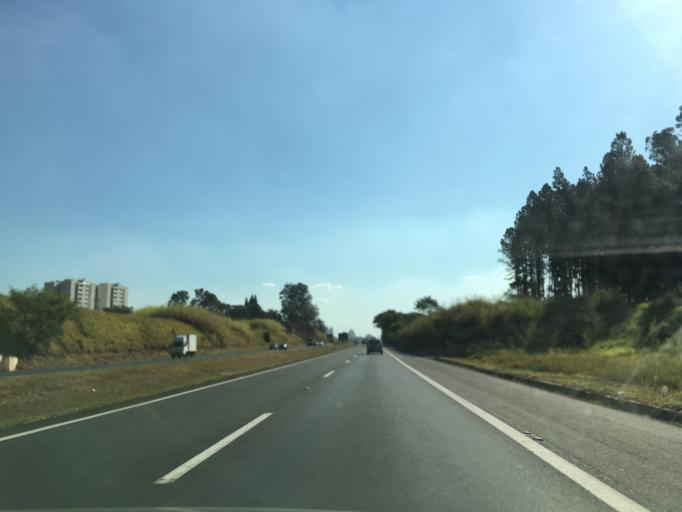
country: BR
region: Sao Paulo
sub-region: Piracicaba
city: Piracicaba
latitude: -22.7211
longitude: -47.6113
